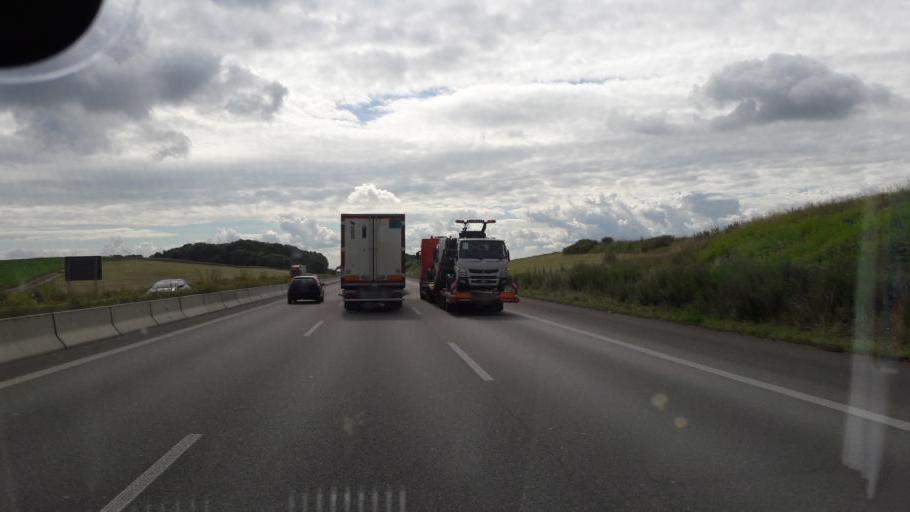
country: DE
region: Baden-Wuerttemberg
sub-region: Regierungsbezirk Stuttgart
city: Kirchardt
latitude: 49.2164
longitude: 9.0067
